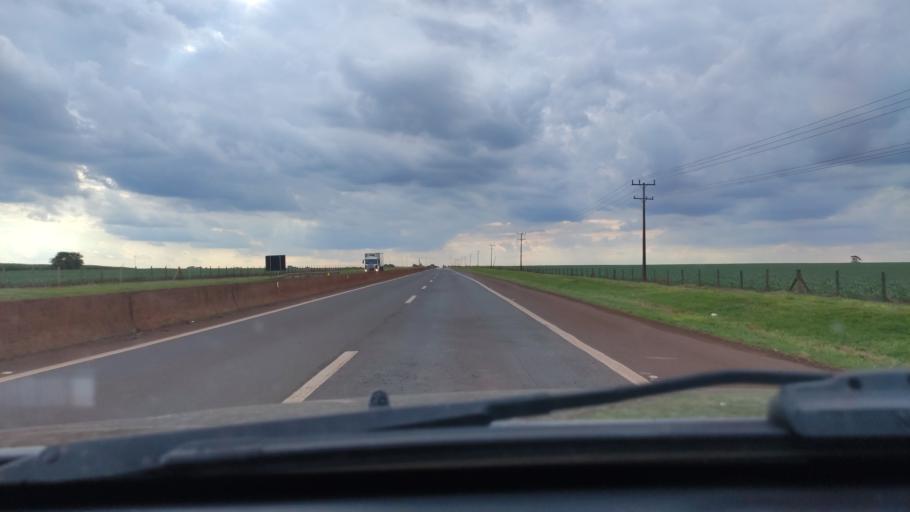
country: BR
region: Sao Paulo
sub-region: Palmital
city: Palmital
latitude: -22.8225
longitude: -50.0402
